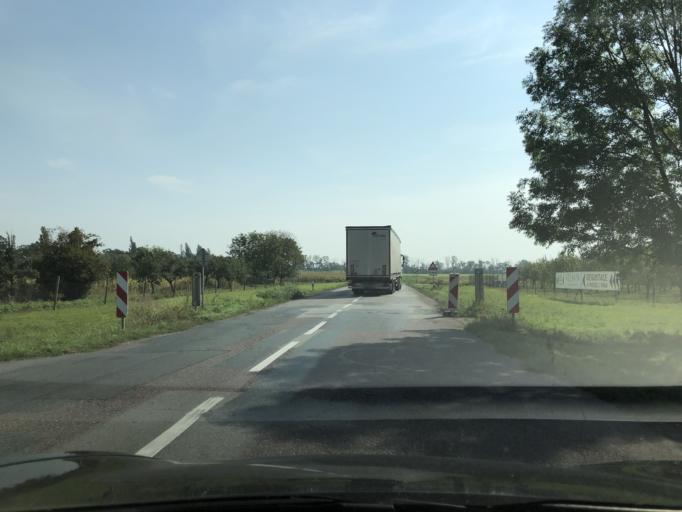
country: CZ
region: South Moravian
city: Brezi
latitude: 48.8261
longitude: 16.5383
